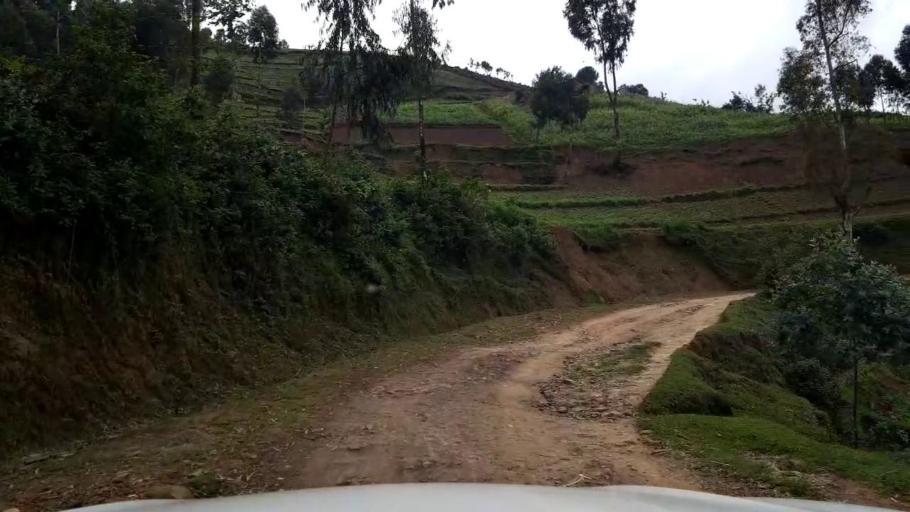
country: RW
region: Western Province
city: Kibuye
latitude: -1.9661
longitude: 29.4854
